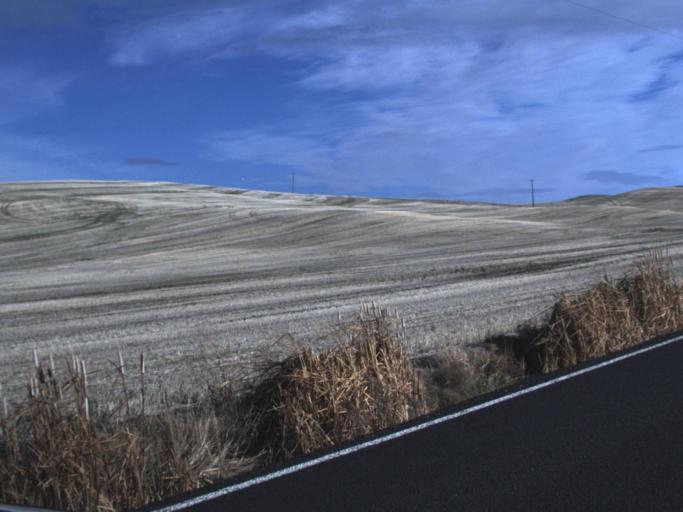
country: US
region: Washington
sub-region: Whitman County
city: Colfax
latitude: 46.9382
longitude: -117.1894
